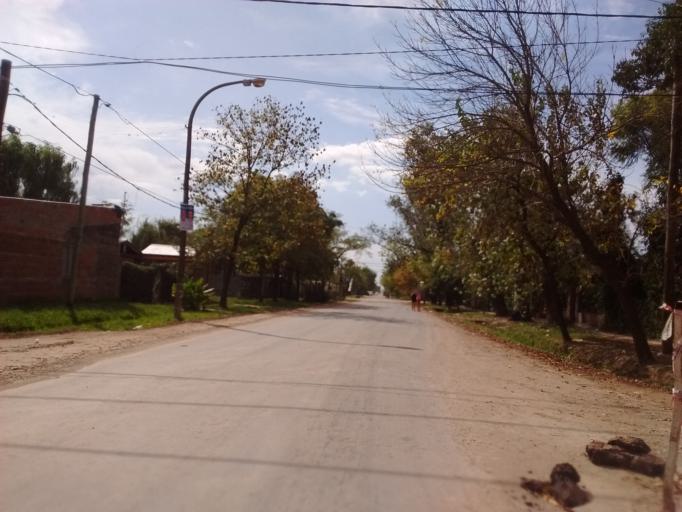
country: AR
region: Santa Fe
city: Funes
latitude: -32.9083
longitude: -60.8131
